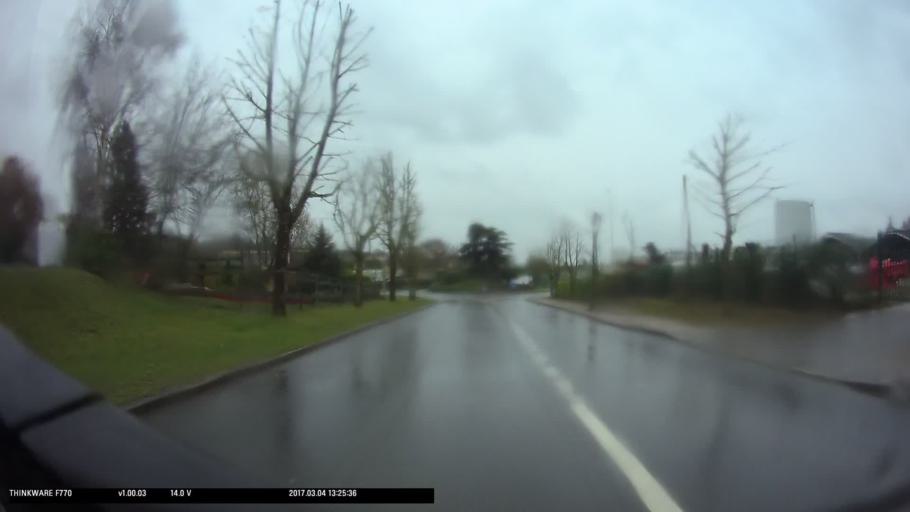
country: FR
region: Ile-de-France
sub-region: Departement du Val-d'Oise
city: Marines
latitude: 49.1447
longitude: 1.9740
